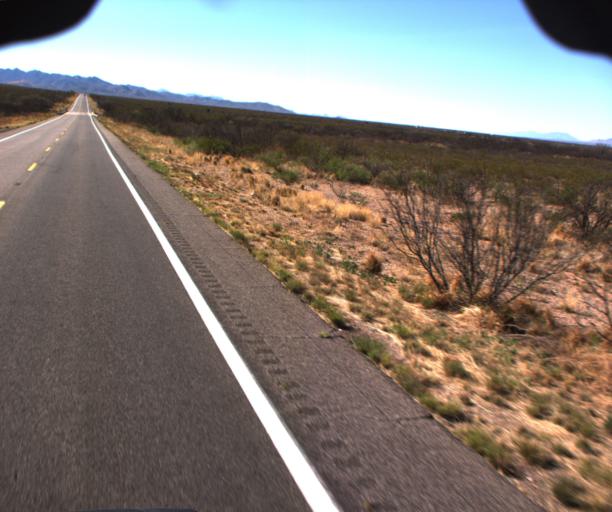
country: US
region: Arizona
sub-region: Cochise County
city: Tombstone
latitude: 31.6115
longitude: -110.0508
